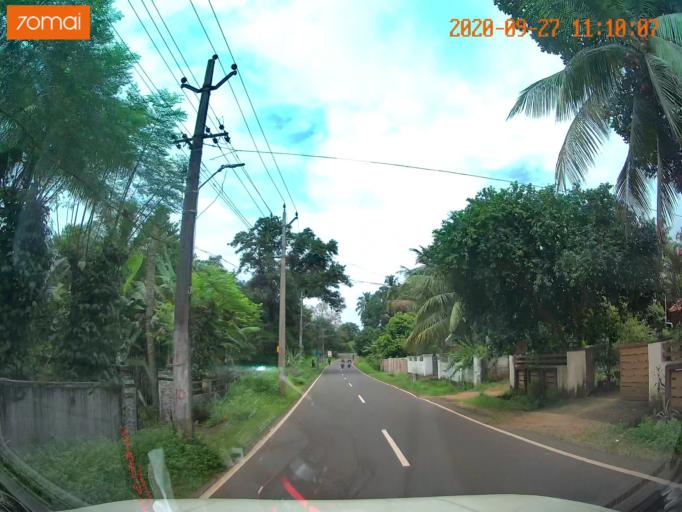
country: IN
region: Kerala
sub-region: Thrissur District
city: Trichur
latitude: 10.4303
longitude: 76.2228
